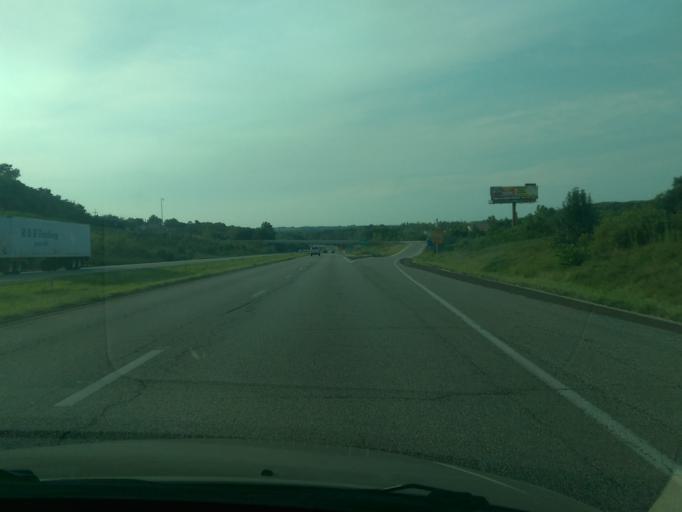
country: US
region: Missouri
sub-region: Platte County
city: Platte City
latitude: 39.3652
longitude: -94.7707
